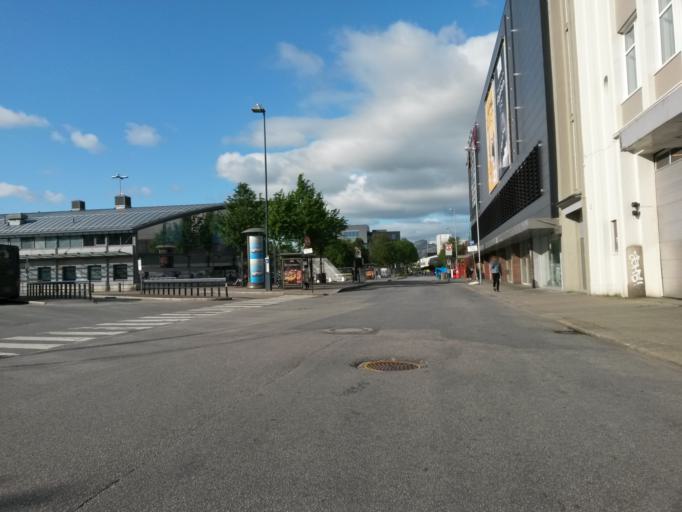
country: NO
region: Rogaland
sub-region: Sandnes
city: Sandnes
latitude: 58.8511
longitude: 5.7371
